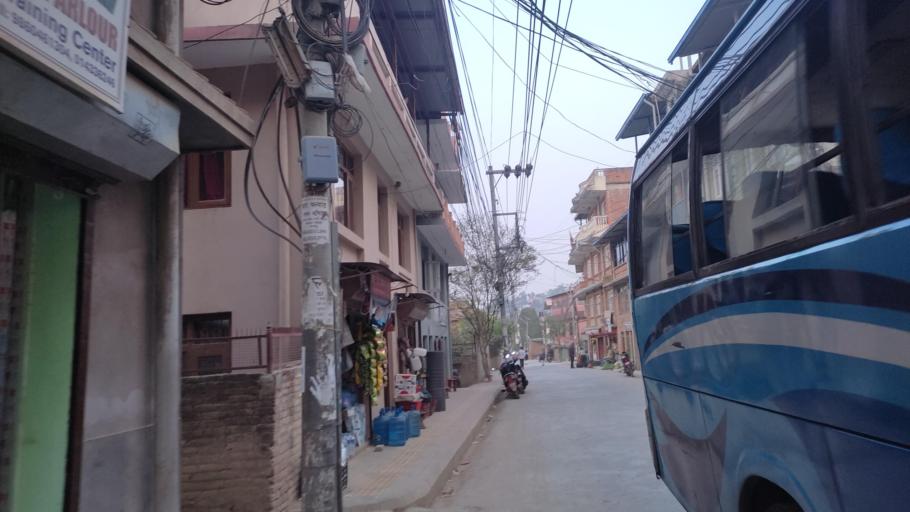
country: NP
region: Central Region
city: Kirtipur
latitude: 27.6699
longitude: 85.2820
